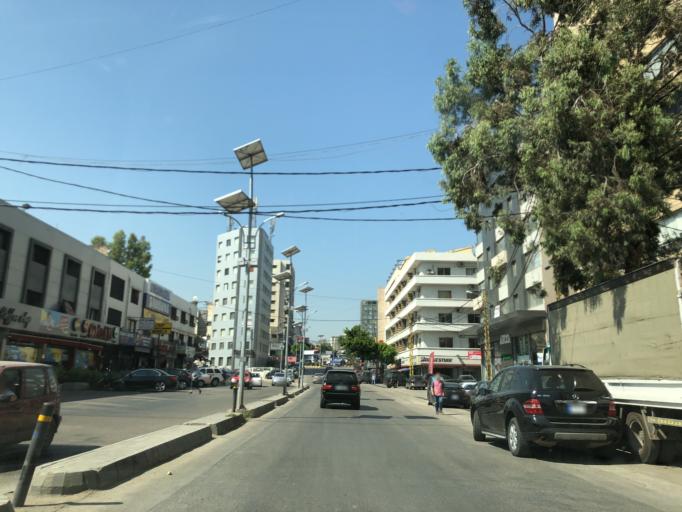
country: LB
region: Mont-Liban
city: Jdaidet el Matn
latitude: 33.8734
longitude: 35.5461
